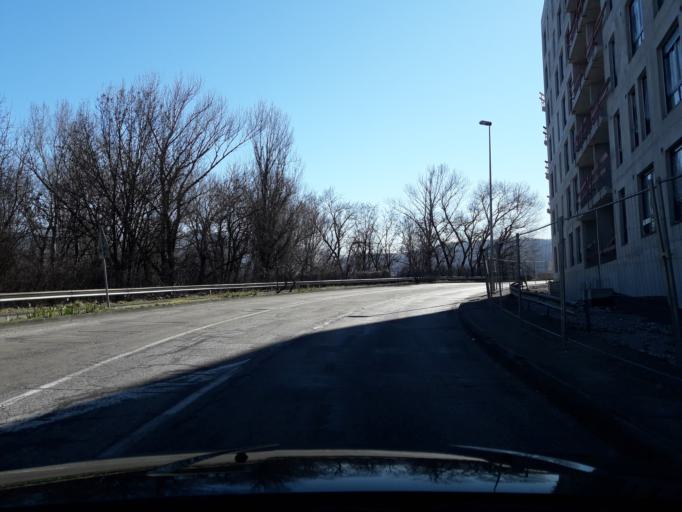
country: FR
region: Rhone-Alpes
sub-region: Departement de l'Isere
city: Echirolles
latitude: 45.1522
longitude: 5.7250
